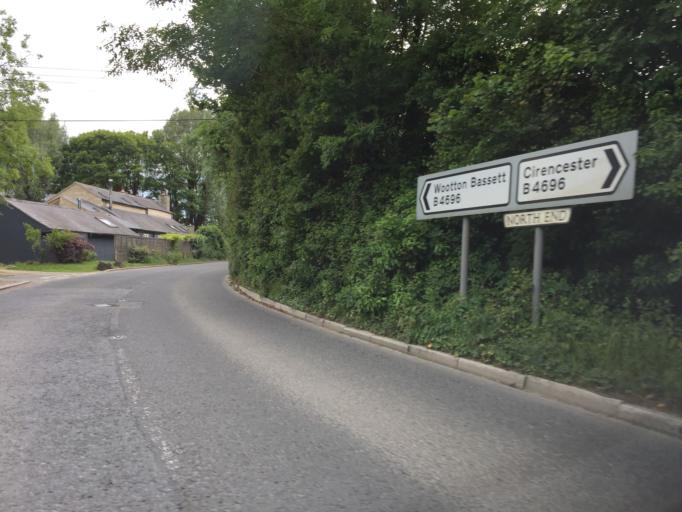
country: GB
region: England
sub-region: Wiltshire
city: Minety
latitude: 51.6518
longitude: -1.9391
